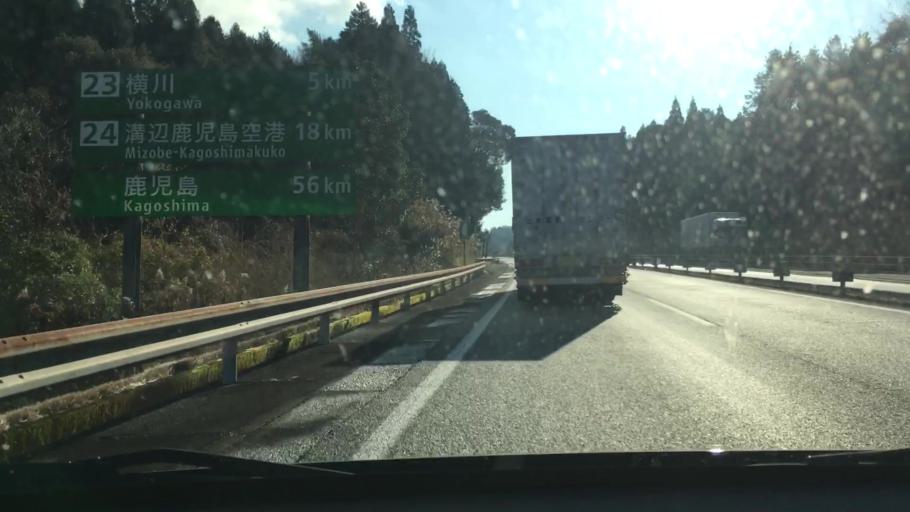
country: JP
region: Kagoshima
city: Okuchi-shinohara
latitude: 31.9368
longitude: 130.7090
